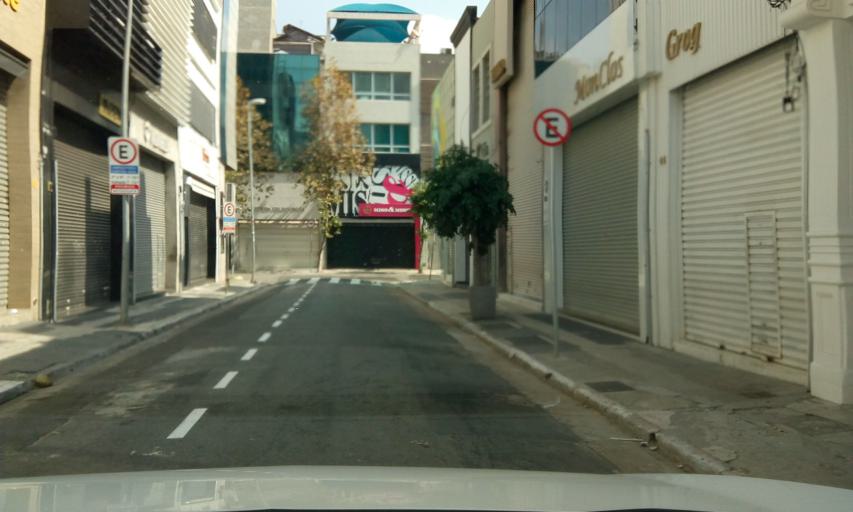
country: BR
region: Sao Paulo
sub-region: Sao Paulo
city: Sao Paulo
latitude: -23.5306
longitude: -46.6397
